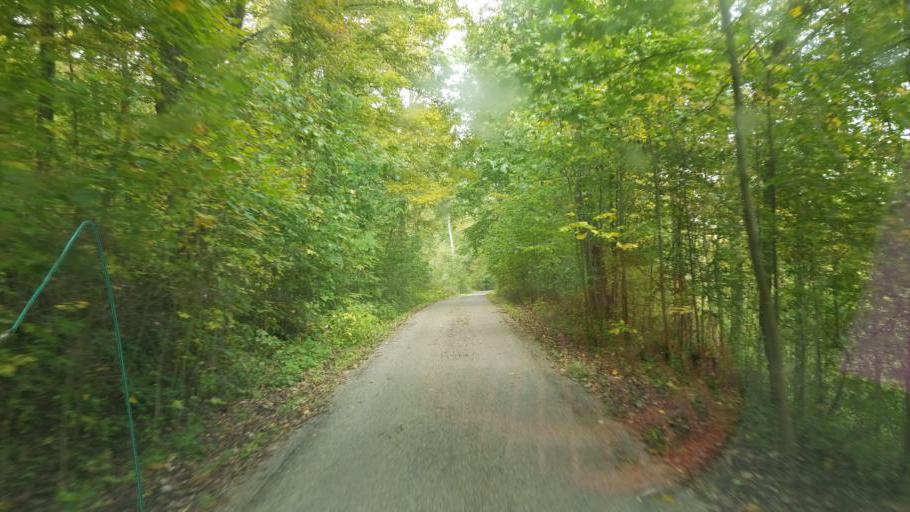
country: US
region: Ohio
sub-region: Richland County
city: Lincoln Heights
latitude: 40.7225
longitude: -82.4055
